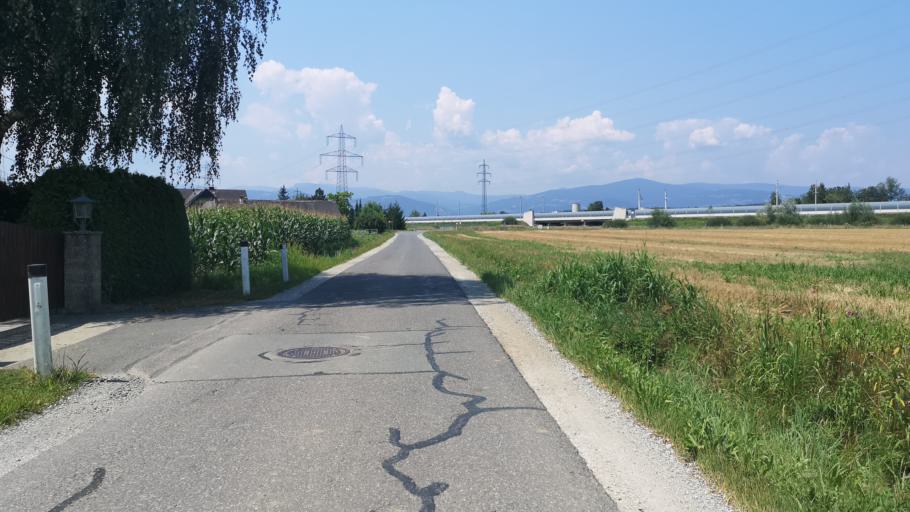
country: AT
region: Styria
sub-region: Politischer Bezirk Deutschlandsberg
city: Gross Sankt Florian
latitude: 46.8145
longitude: 15.3276
